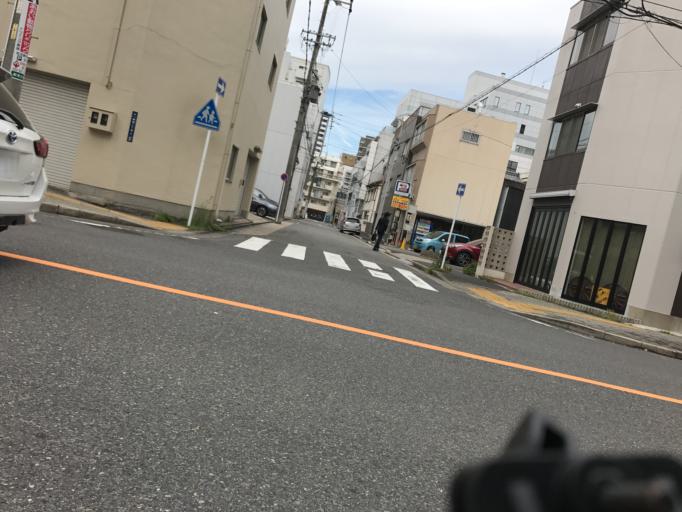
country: JP
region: Aichi
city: Nagoya-shi
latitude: 35.1692
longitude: 136.9243
